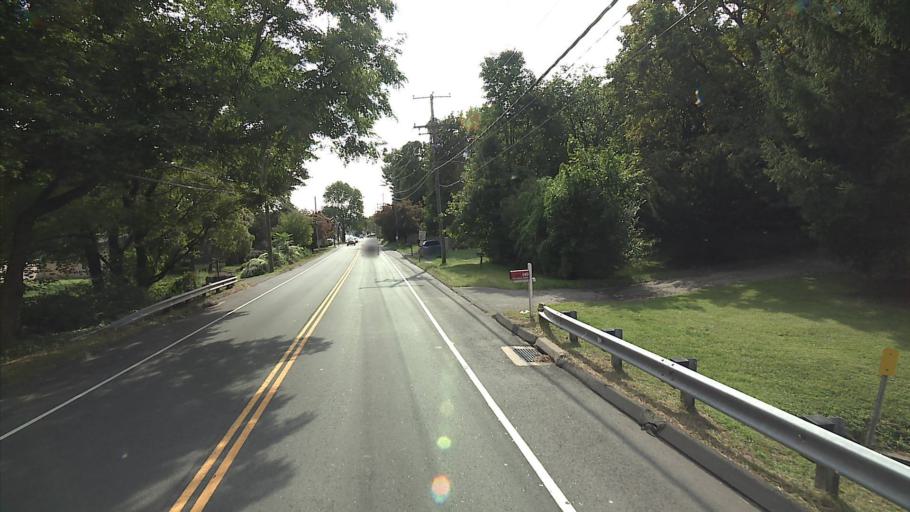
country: US
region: Connecticut
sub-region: Fairfield County
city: Norwalk
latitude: 41.1288
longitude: -73.4383
